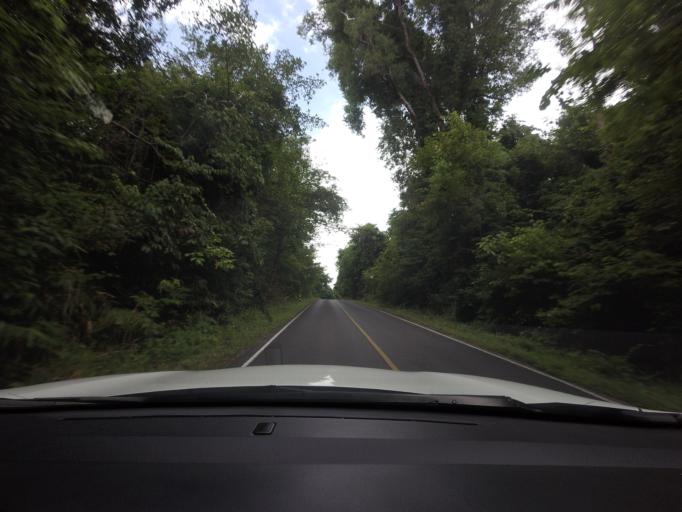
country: TH
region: Nakhon Nayok
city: Pak Phli
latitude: 14.2510
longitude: 101.3833
